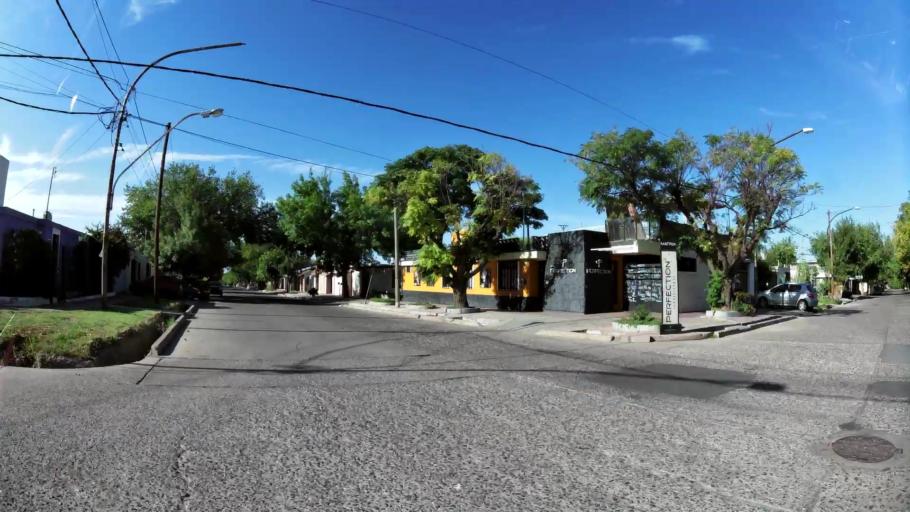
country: AR
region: Mendoza
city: Mendoza
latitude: -32.9080
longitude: -68.8239
